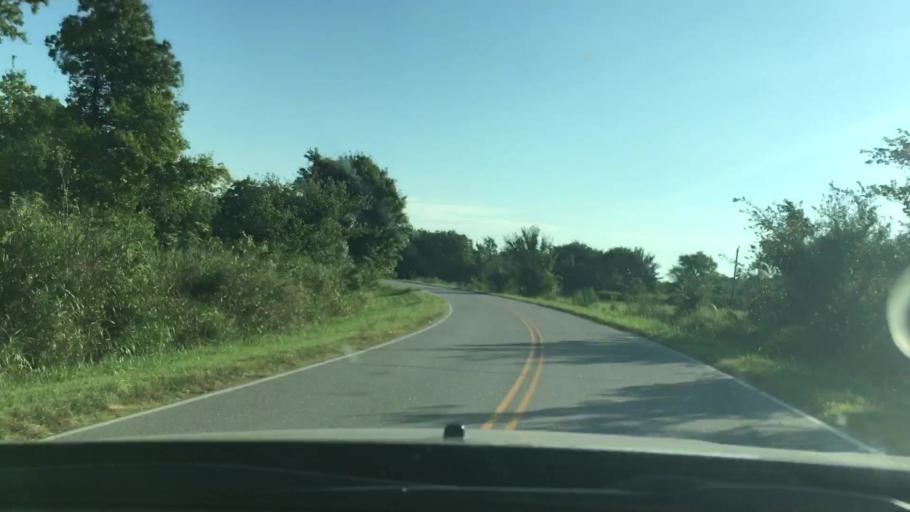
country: US
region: Oklahoma
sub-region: Pontotoc County
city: Ada
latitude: 34.6950
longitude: -96.4431
